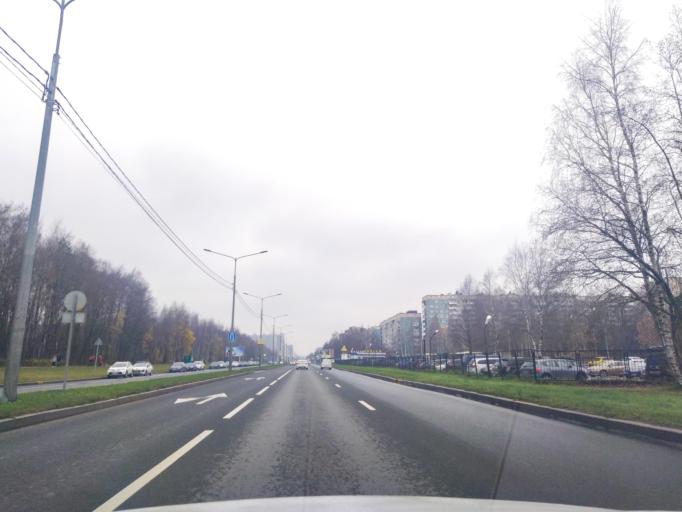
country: RU
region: St.-Petersburg
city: Sosnovka
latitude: 60.0321
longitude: 30.3595
